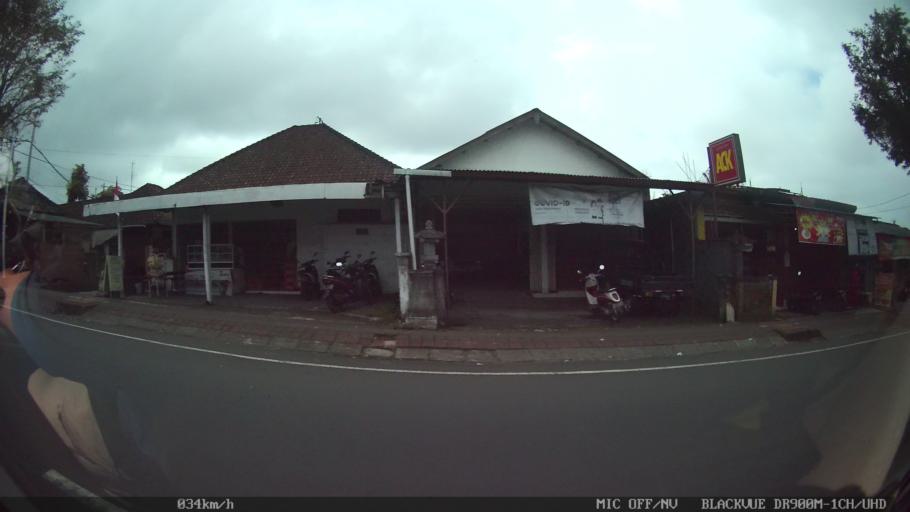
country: ID
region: Bali
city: Bangli
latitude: -8.4554
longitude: 115.3531
